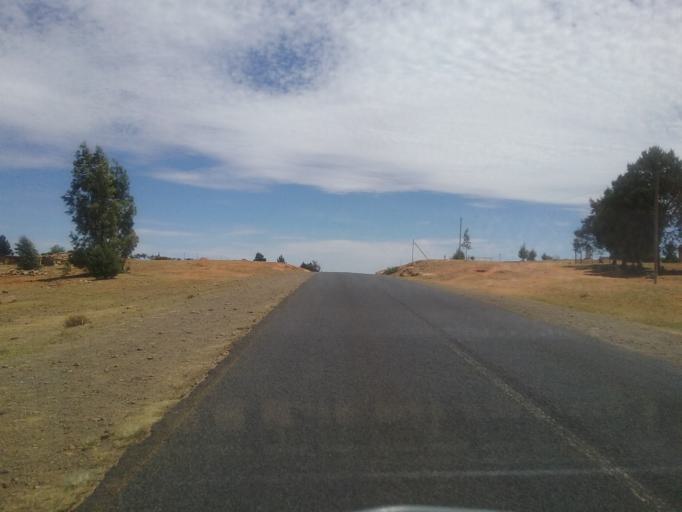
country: LS
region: Mafeteng
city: Mafeteng
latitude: -29.8838
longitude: 27.2466
